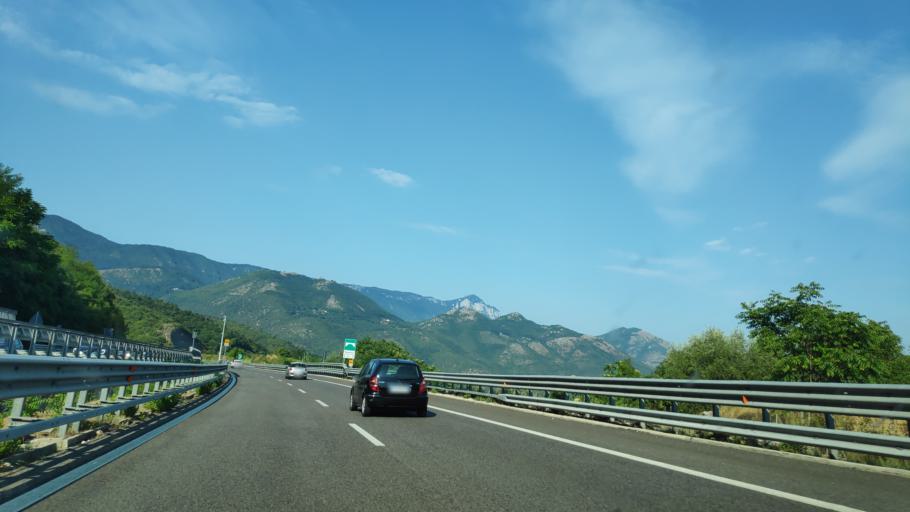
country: IT
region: Campania
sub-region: Provincia di Salerno
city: Pertosa
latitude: 40.5335
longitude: 15.4595
